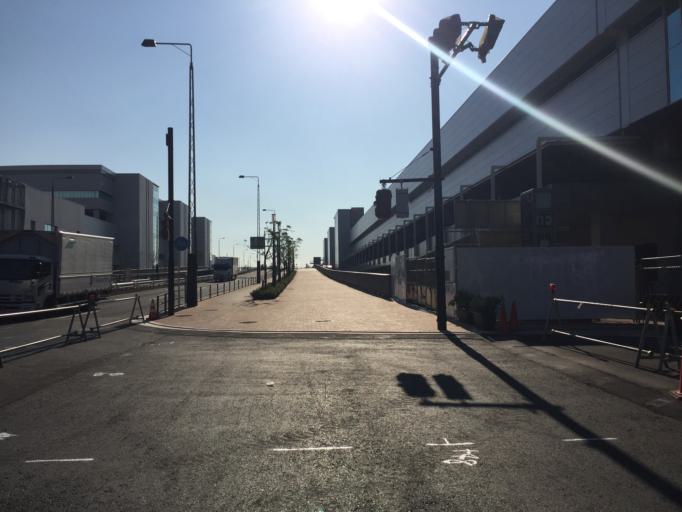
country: JP
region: Tokyo
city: Tokyo
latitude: 35.6442
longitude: 139.7832
